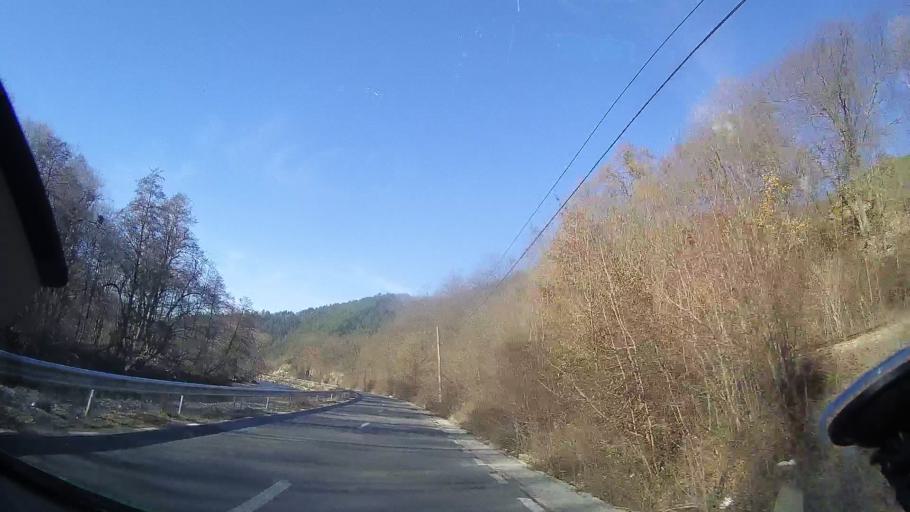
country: RO
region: Bihor
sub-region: Comuna Bratca
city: Bratca
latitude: 46.9287
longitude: 22.6452
